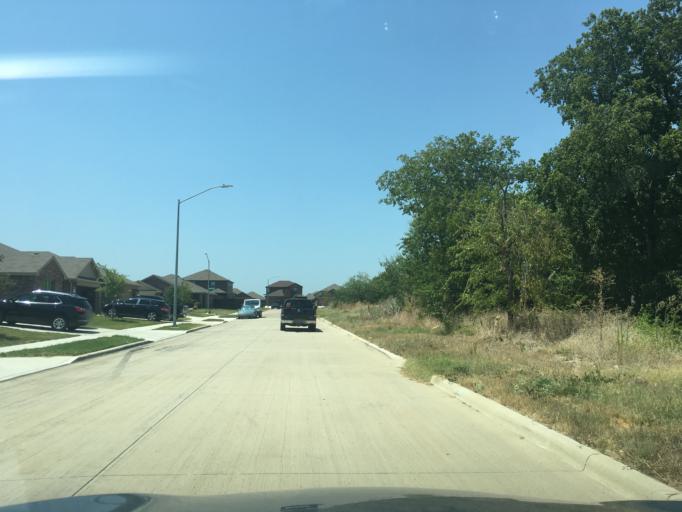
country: US
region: Texas
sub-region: Tarrant County
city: Crowley
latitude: 32.6142
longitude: -97.3610
